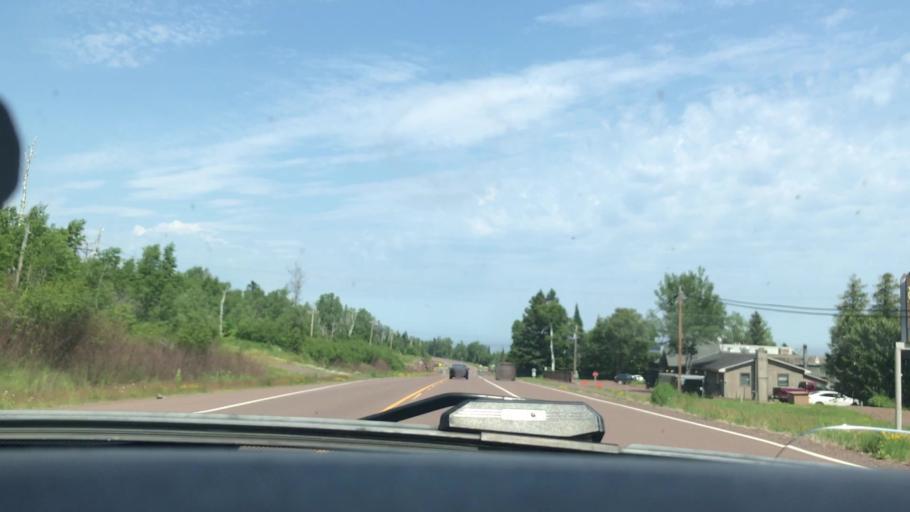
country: US
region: Minnesota
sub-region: Cook County
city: Grand Marais
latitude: 47.6073
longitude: -90.7757
